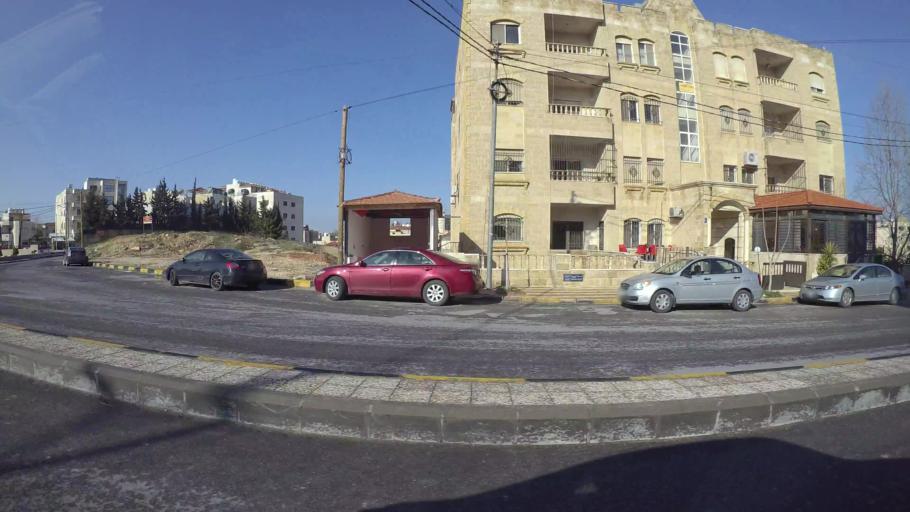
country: JO
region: Amman
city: Al Jubayhah
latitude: 32.0065
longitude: 35.8508
